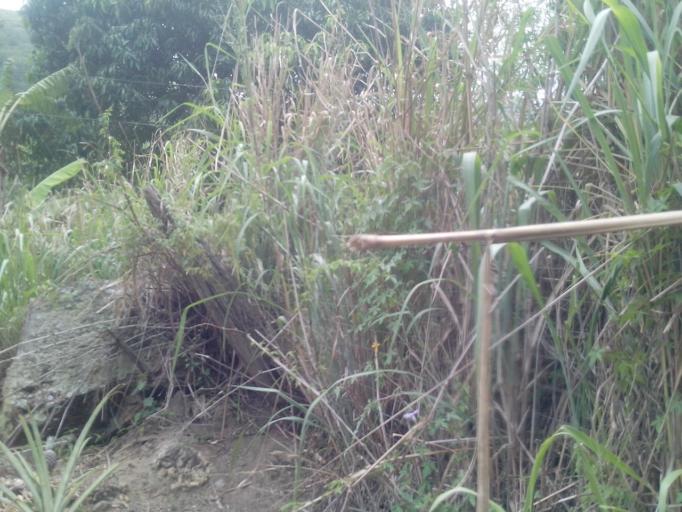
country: BR
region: Rio de Janeiro
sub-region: Miguel Pereira
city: Miguel Pereira
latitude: -22.4894
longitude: -43.4518
